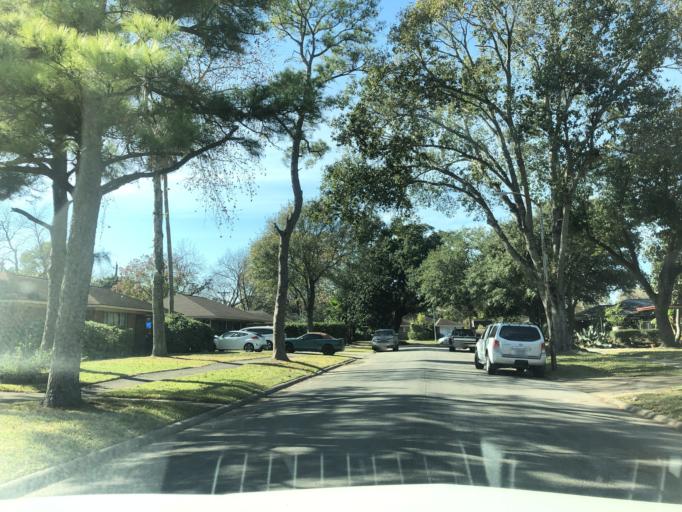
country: US
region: Texas
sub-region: Harris County
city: Bellaire
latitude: 29.6823
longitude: -95.5071
